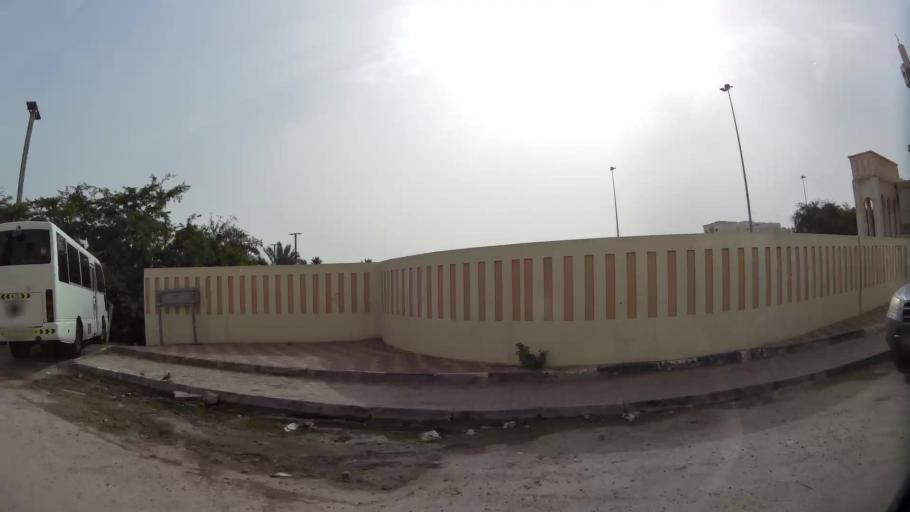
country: QA
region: Baladiyat ad Dawhah
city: Doha
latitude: 25.2828
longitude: 51.5510
